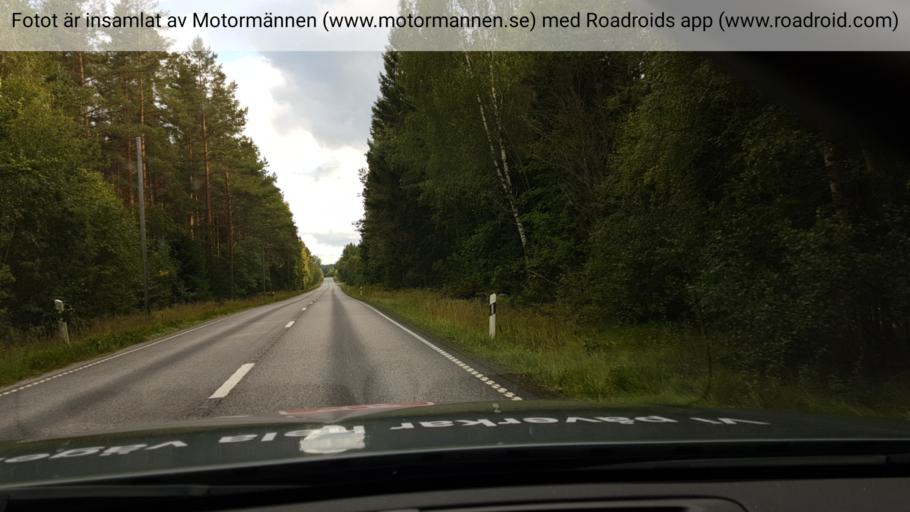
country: SE
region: Stockholm
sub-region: Norrtalje Kommun
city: Hallstavik
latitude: 59.9862
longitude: 18.5950
